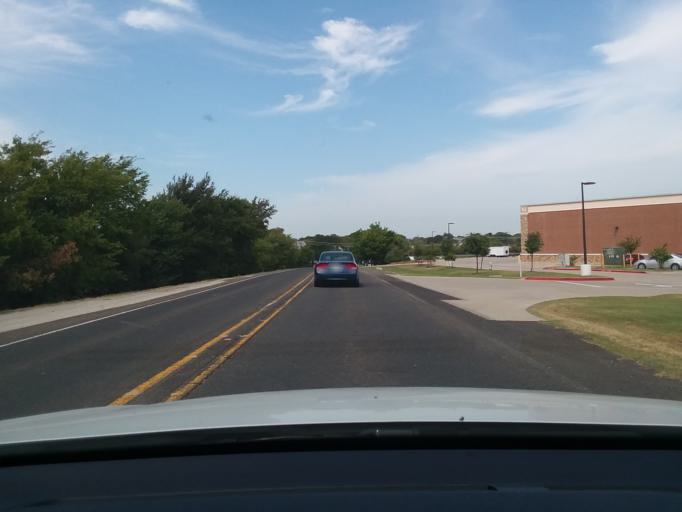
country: US
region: Texas
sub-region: Denton County
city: Bartonville
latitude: 33.0740
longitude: -97.1290
